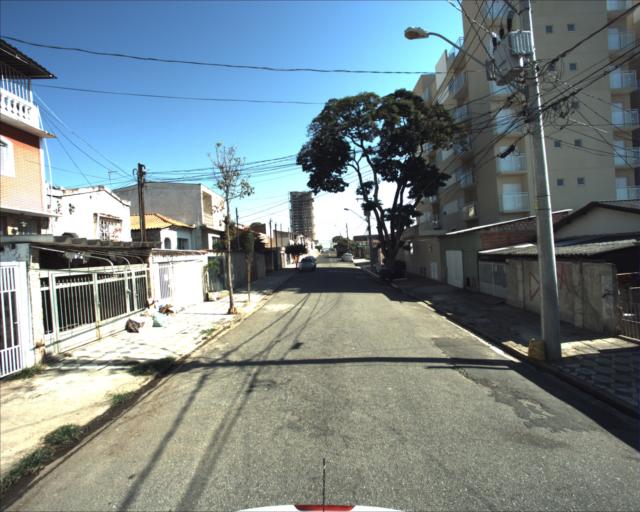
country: BR
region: Sao Paulo
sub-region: Sorocaba
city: Sorocaba
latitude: -23.5062
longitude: -47.4405
